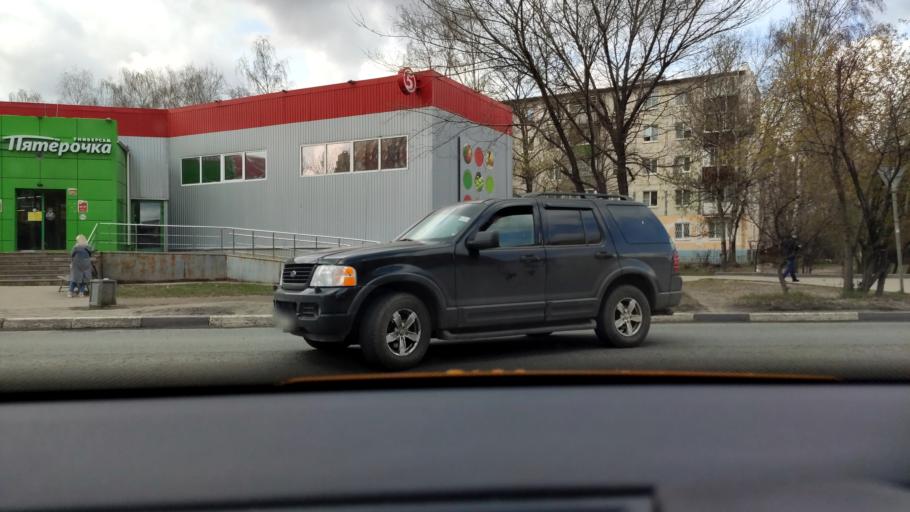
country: RU
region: Moskovskaya
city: Zheleznodorozhnyy
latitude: 55.7415
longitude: 38.0305
